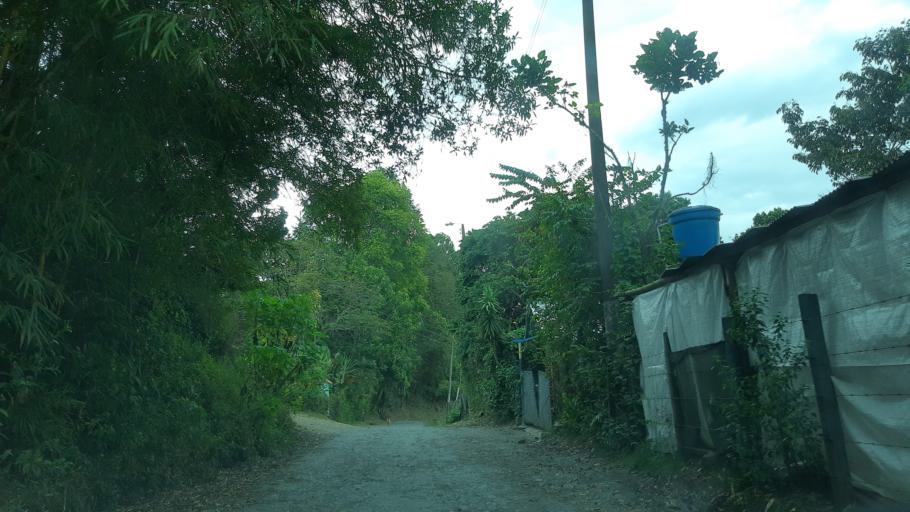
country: CO
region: Boyaca
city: Chivor
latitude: 4.9754
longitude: -73.3204
